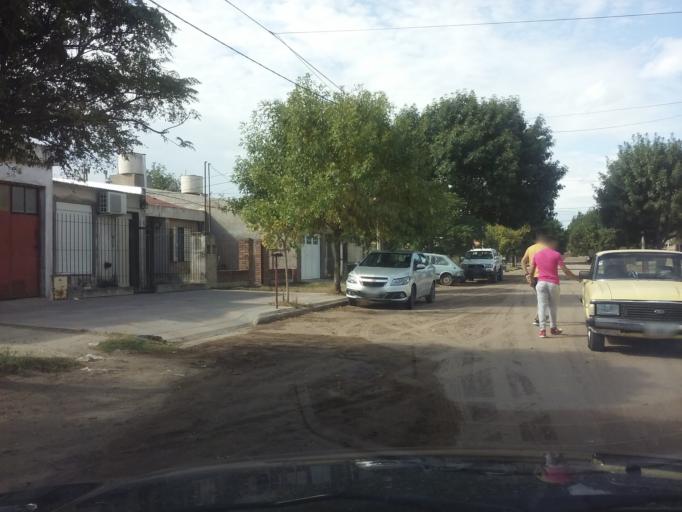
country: AR
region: La Pampa
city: Santa Rosa
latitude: -36.6502
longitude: -64.2950
